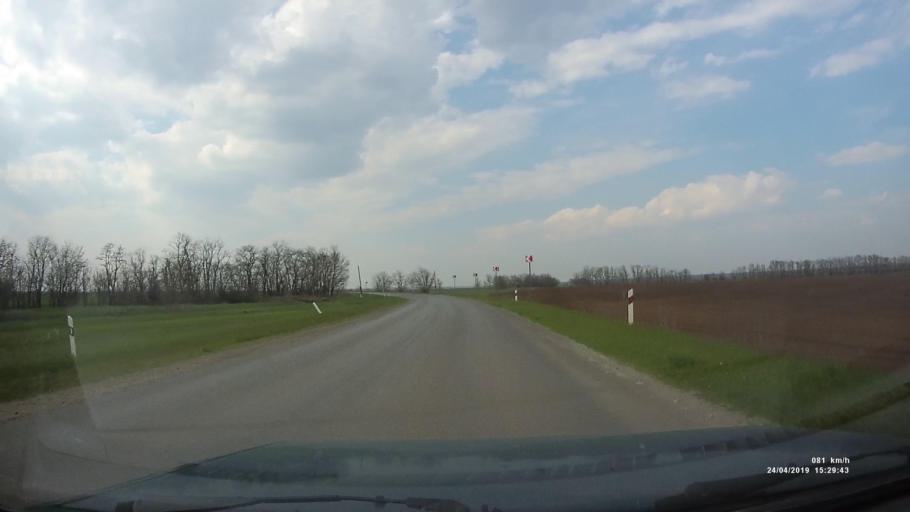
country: RU
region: Rostov
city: Remontnoye
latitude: 46.5964
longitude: 43.0158
